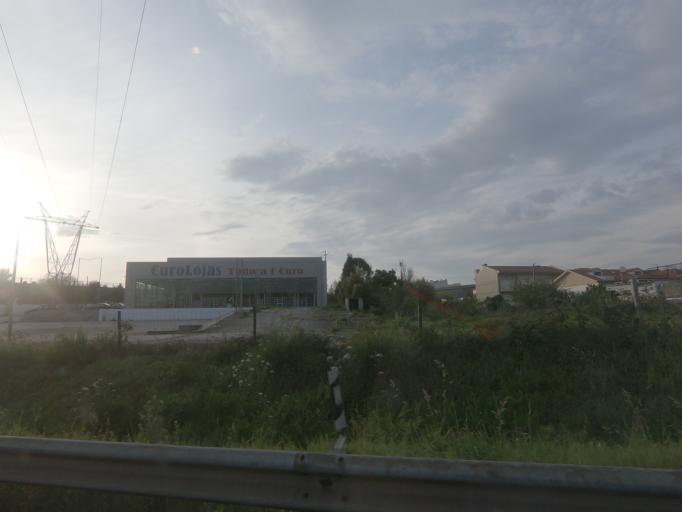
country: PT
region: Porto
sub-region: Gondomar
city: Baguim do Monte
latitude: 41.2027
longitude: -8.5520
